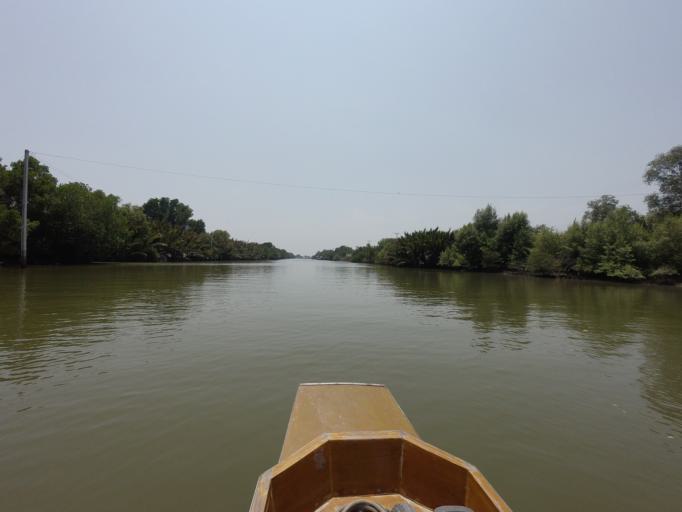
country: TH
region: Bangkok
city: Thung Khru
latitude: 13.5424
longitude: 100.4579
